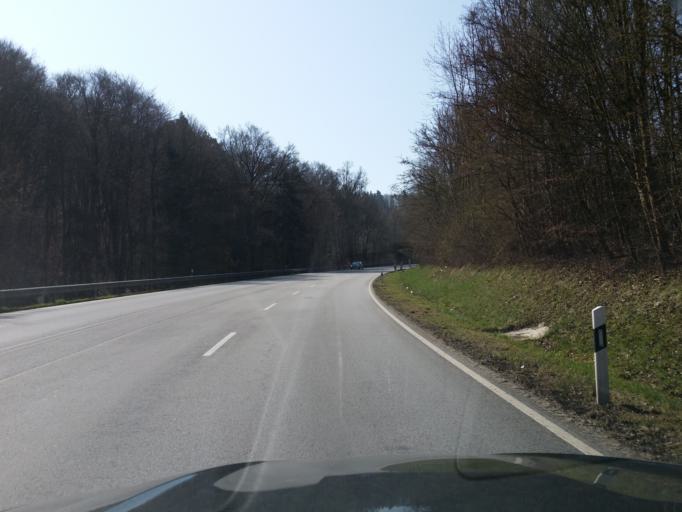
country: DE
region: Bavaria
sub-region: Lower Bavaria
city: Landshut
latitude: 48.5426
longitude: 12.1848
